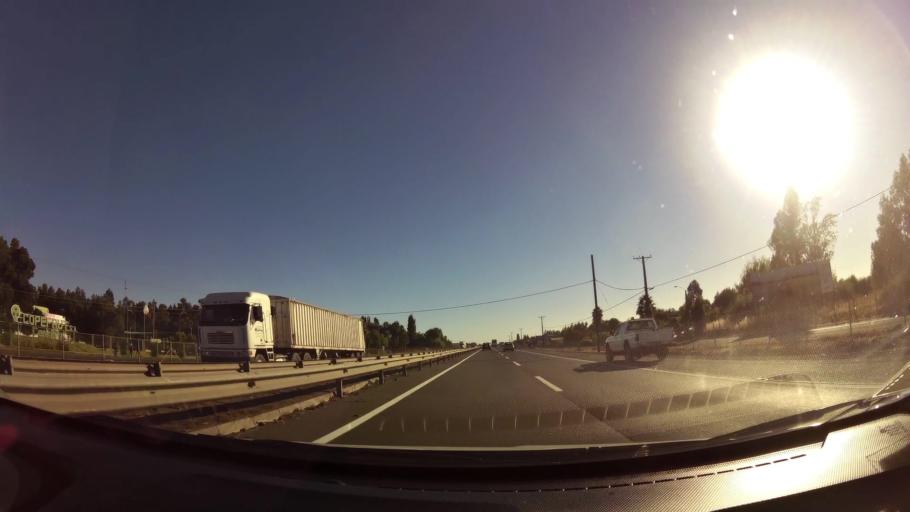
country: CL
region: Maule
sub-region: Provincia de Curico
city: Teno
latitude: -34.8444
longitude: -71.1070
